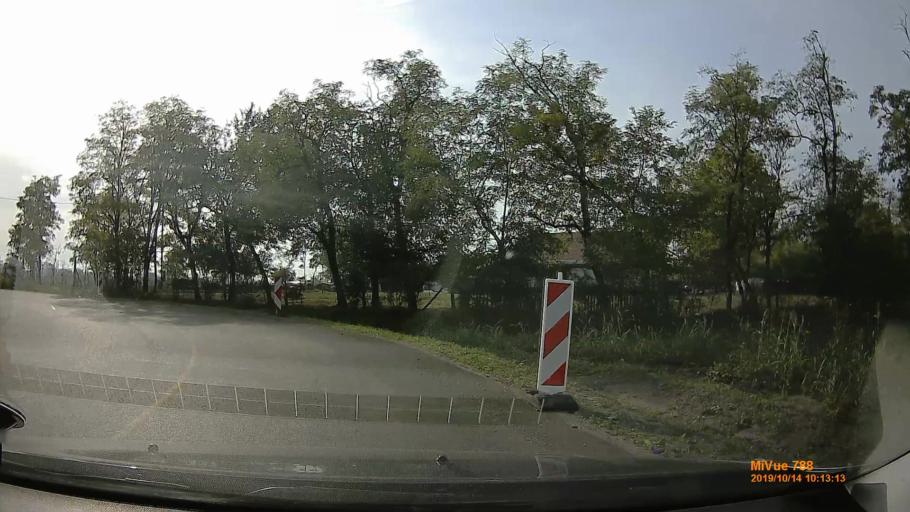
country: HU
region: Pest
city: Tortel
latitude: 47.1870
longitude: 19.9248
